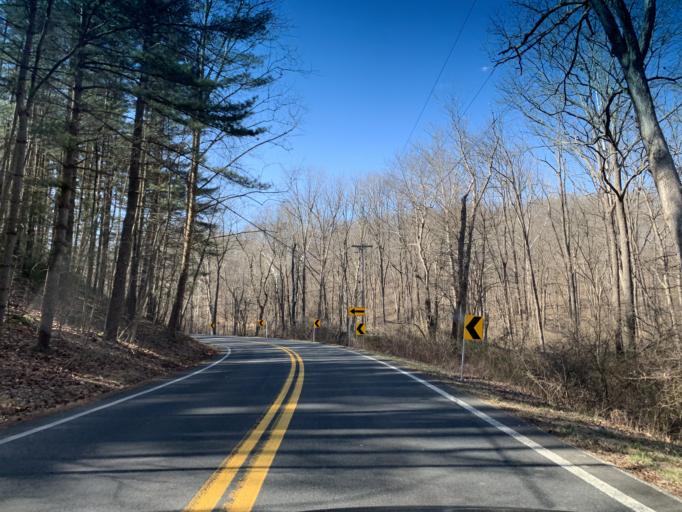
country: US
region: Maryland
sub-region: Carroll County
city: Hampstead
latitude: 39.5757
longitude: -76.8917
